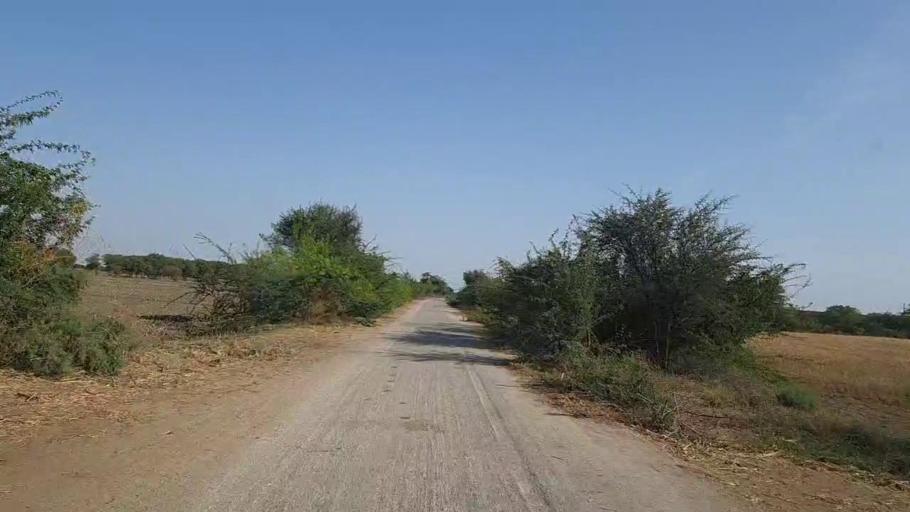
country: PK
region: Sindh
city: Kotri
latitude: 25.1472
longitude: 68.2956
